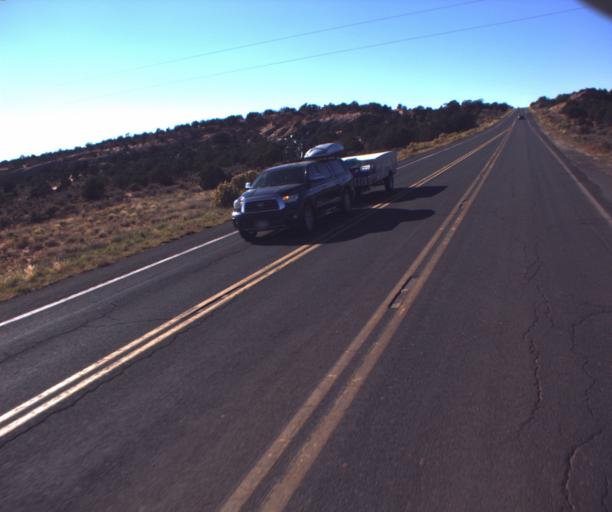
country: US
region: Arizona
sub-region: Coconino County
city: Kaibito
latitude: 36.5810
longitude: -110.7967
